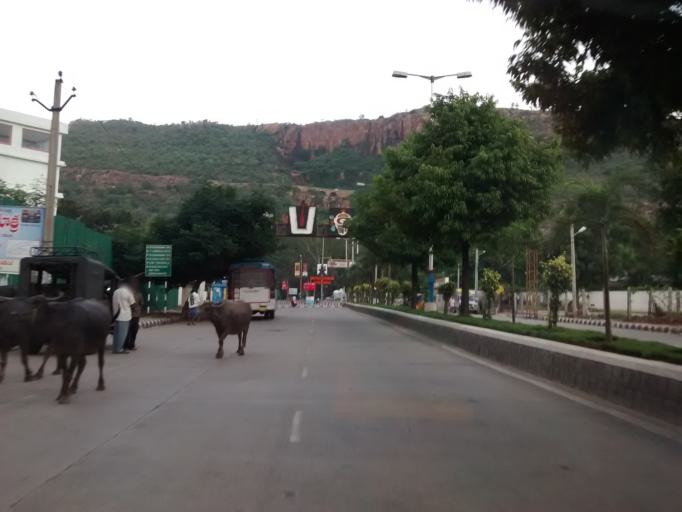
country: IN
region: Andhra Pradesh
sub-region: Chittoor
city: Akkarampalle
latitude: 13.6530
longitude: 79.4212
